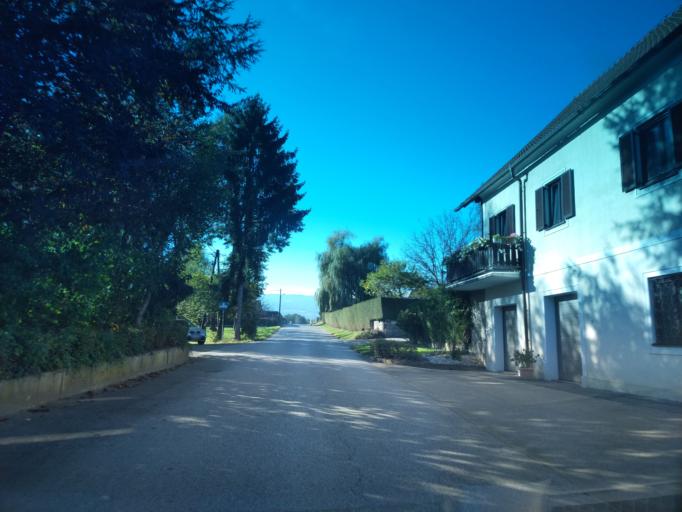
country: AT
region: Styria
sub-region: Politischer Bezirk Deutschlandsberg
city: Stallhof
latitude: 46.8885
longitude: 15.2967
